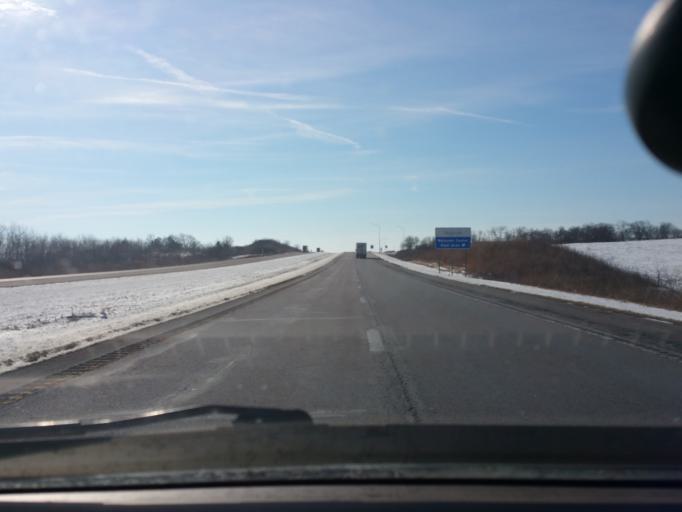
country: US
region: Iowa
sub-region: Decatur County
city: Lamoni
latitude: 40.5555
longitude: -93.9519
